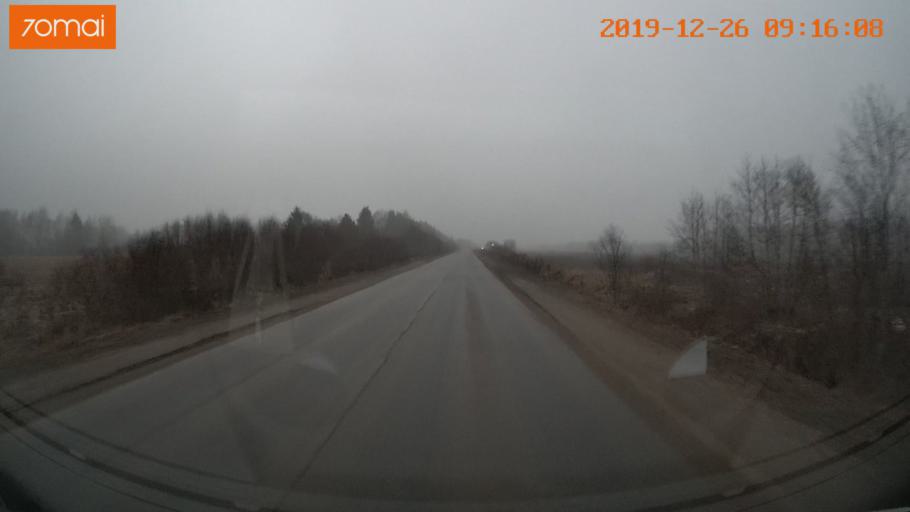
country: RU
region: Vologda
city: Gryazovets
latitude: 58.9139
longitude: 40.2386
